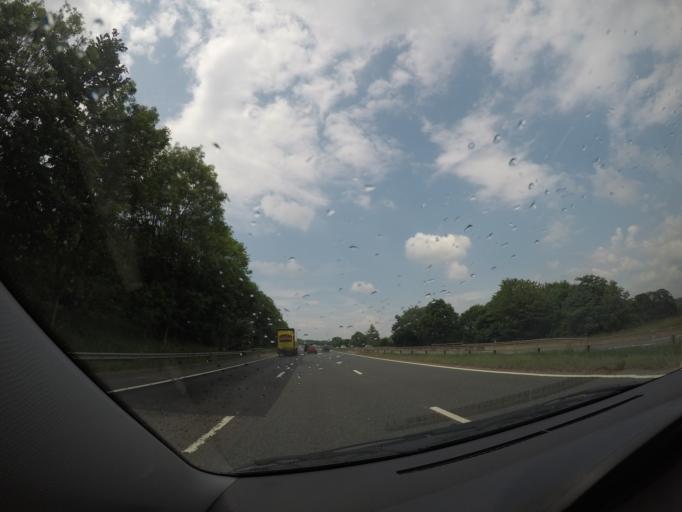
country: GB
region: England
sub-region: Cumbria
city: Penrith
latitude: 54.7553
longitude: -2.8210
